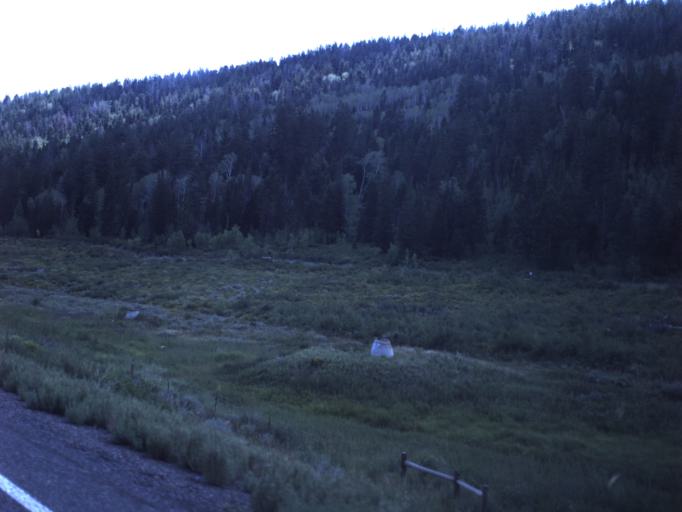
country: US
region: Utah
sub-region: Carbon County
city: Helper
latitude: 39.8565
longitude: -111.0883
